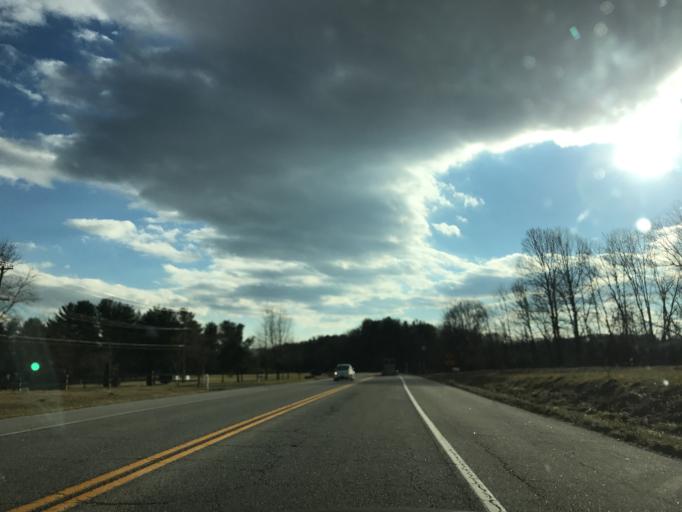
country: US
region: Maryland
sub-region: Cecil County
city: Rising Sun
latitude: 39.6681
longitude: -76.0749
